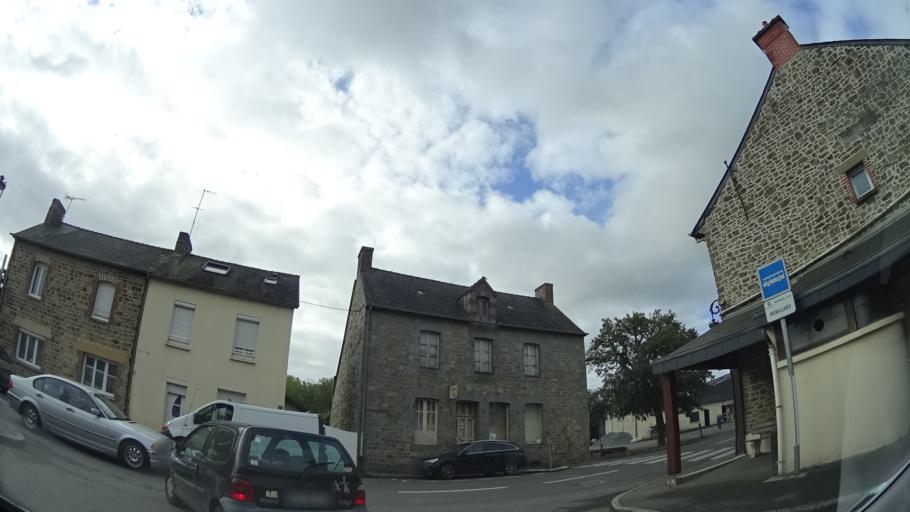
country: FR
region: Brittany
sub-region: Departement d'Ille-et-Vilaine
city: Montreuil-sur-Ille
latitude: 48.3069
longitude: -1.6723
